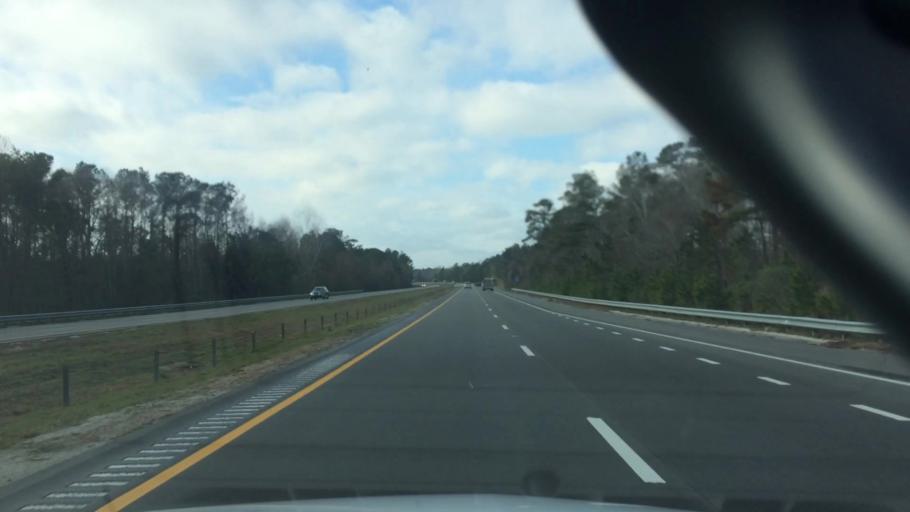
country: US
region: North Carolina
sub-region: New Hanover County
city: Wrightsboro
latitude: 34.3180
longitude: -77.9259
